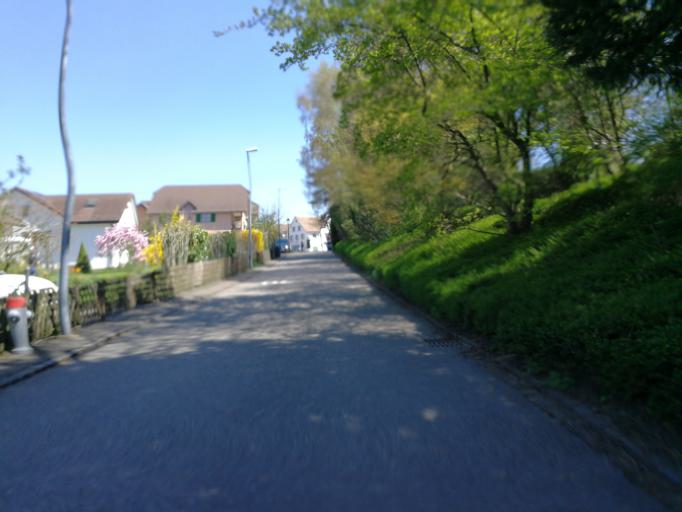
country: CH
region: Zurich
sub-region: Bezirk Meilen
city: Uetikon
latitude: 47.2626
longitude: 8.6755
